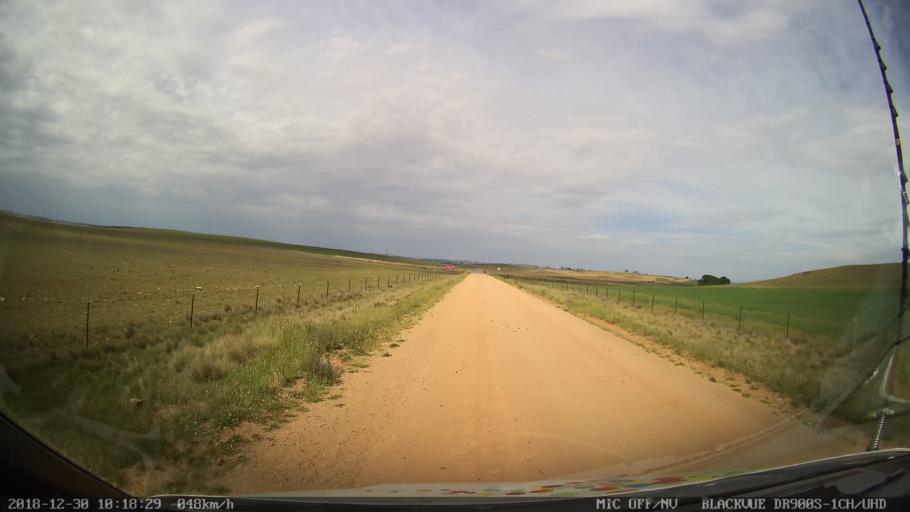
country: AU
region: New South Wales
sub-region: Snowy River
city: Berridale
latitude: -36.5521
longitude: 149.0090
